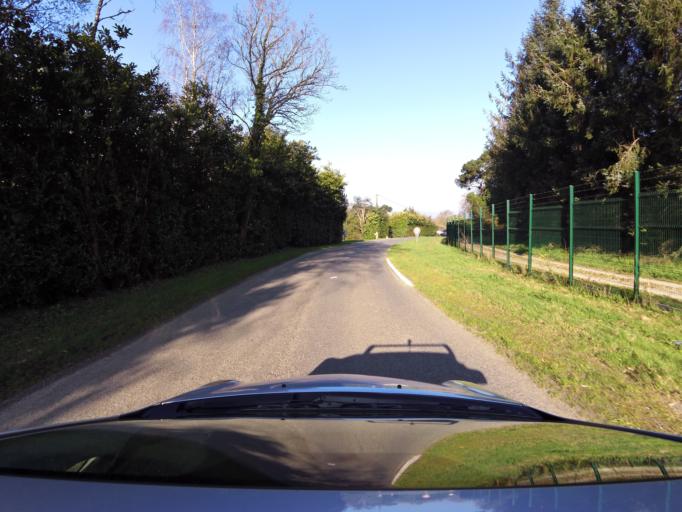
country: FR
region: Brittany
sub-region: Departement du Morbihan
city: Ploemeur
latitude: 47.7429
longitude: -3.4620
